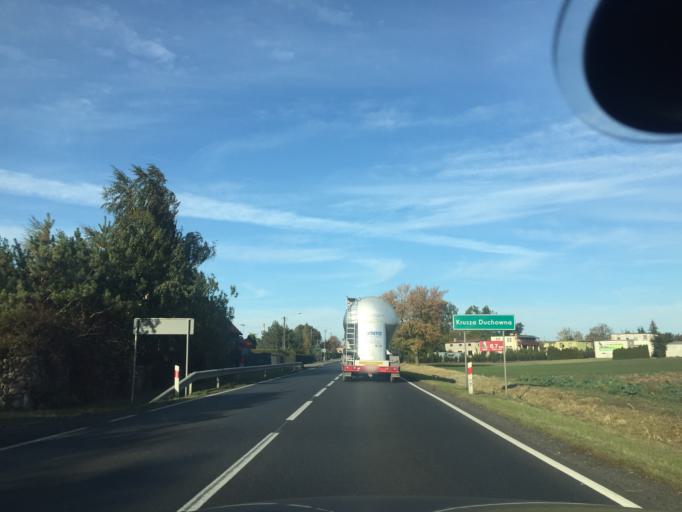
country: PL
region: Kujawsko-Pomorskie
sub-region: Powiat inowroclawski
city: Inowroclaw
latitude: 52.7293
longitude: 18.2327
